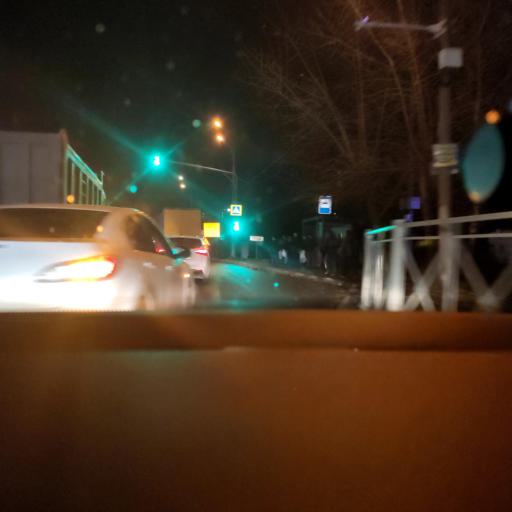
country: RU
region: Moskovskaya
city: Kotel'niki
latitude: 55.6387
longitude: 37.8266
